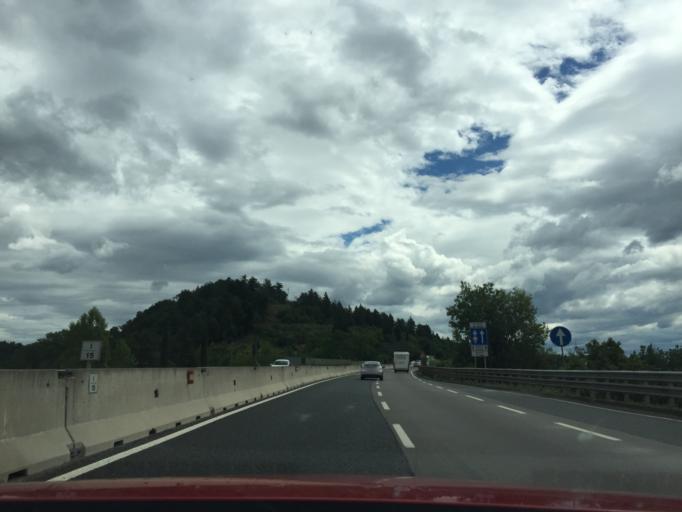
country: IT
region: Tuscany
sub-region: Province of Florence
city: Ginestra Fiorentina
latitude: 43.7123
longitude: 11.0588
